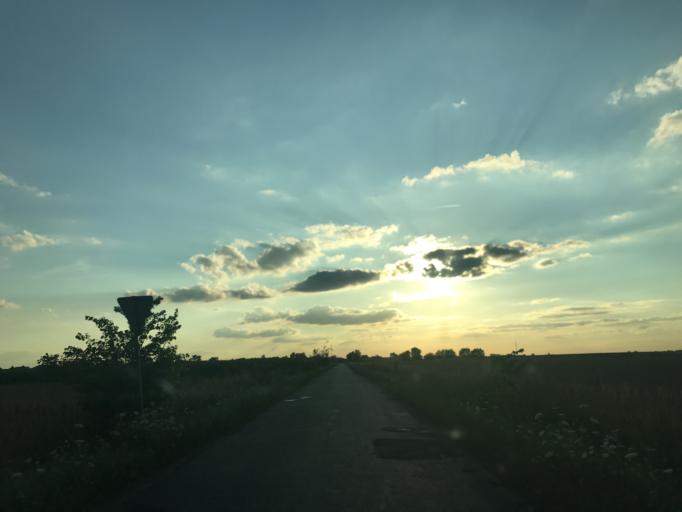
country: PL
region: Greater Poland Voivodeship
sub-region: Powiat gostynski
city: Pepowo
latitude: 51.8191
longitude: 17.0966
